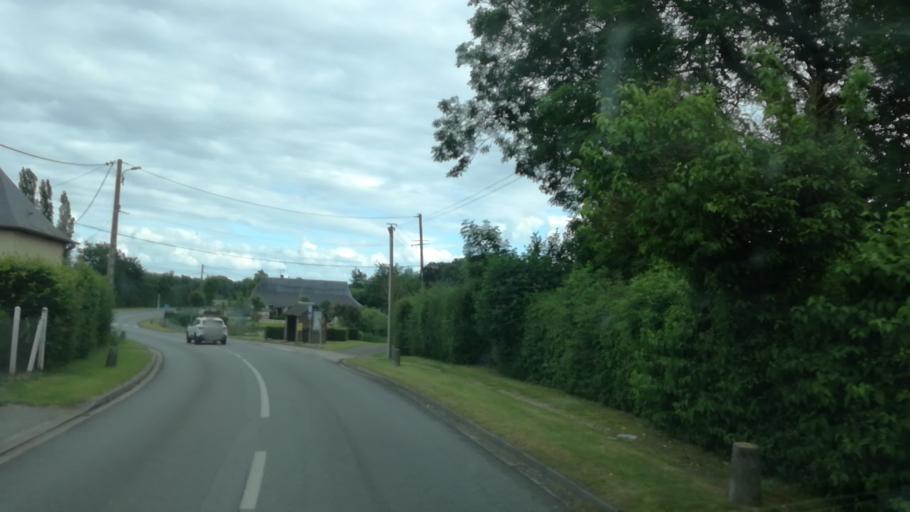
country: FR
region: Haute-Normandie
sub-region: Departement de l'Eure
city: Le Neubourg
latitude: 49.2115
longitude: 0.8499
